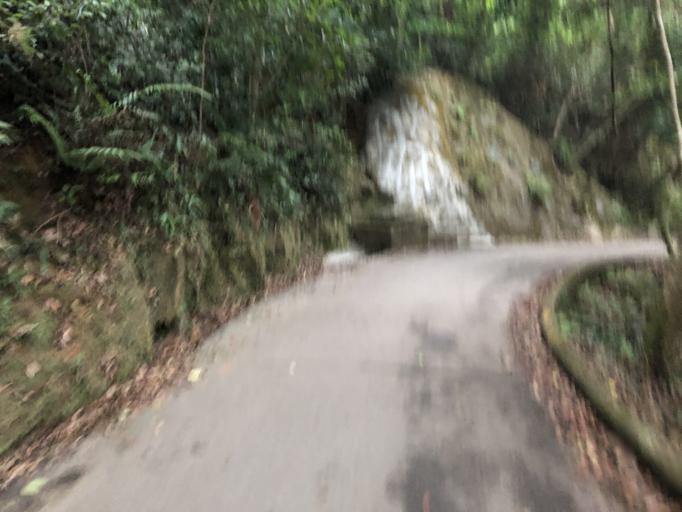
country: HK
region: Wanchai
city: Wan Chai
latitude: 22.2658
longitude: 114.2144
